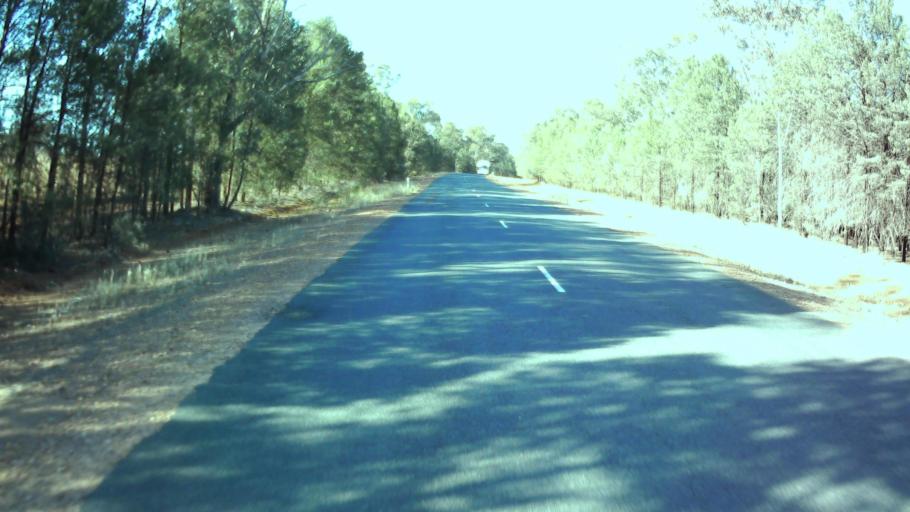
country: AU
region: New South Wales
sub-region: Weddin
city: Grenfell
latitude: -34.0287
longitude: 148.0949
